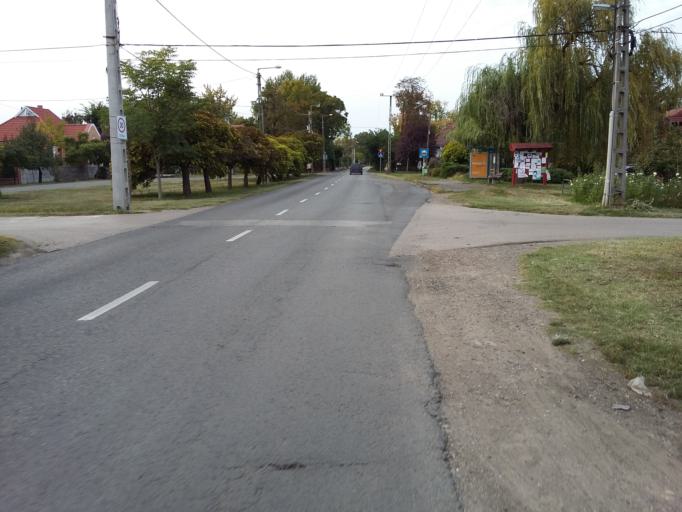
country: HU
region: Csongrad
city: Szeged
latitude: 46.2280
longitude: 20.1162
